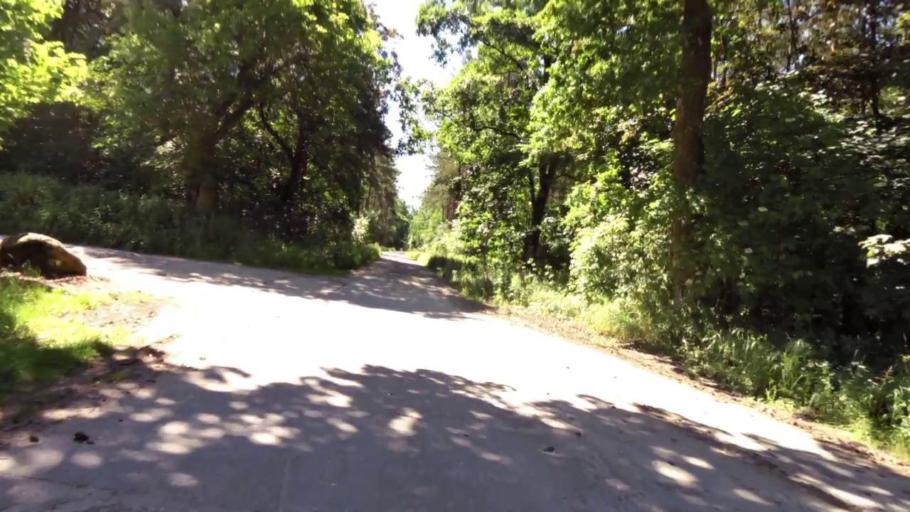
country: PL
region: West Pomeranian Voivodeship
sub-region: Powiat swidwinski
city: Rabino
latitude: 53.9229
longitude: 16.0087
